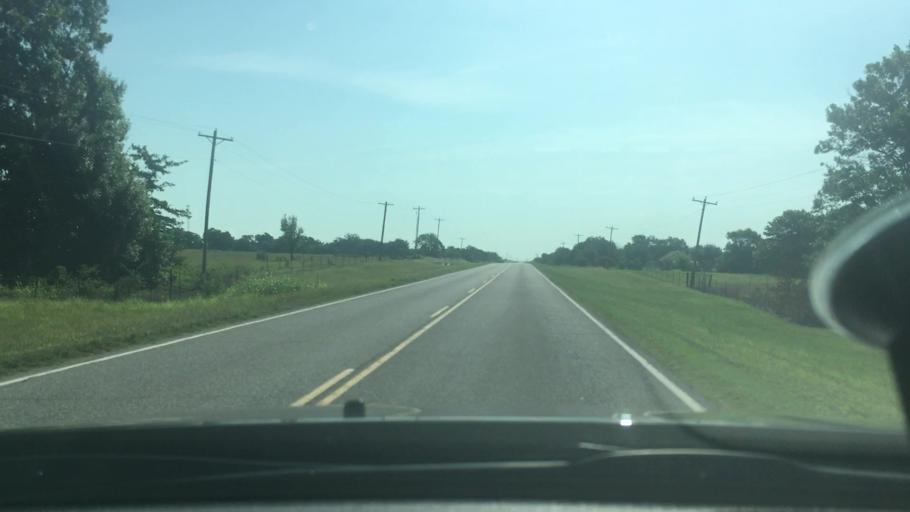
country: US
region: Oklahoma
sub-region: Garvin County
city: Wynnewood
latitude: 34.6518
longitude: -97.2584
